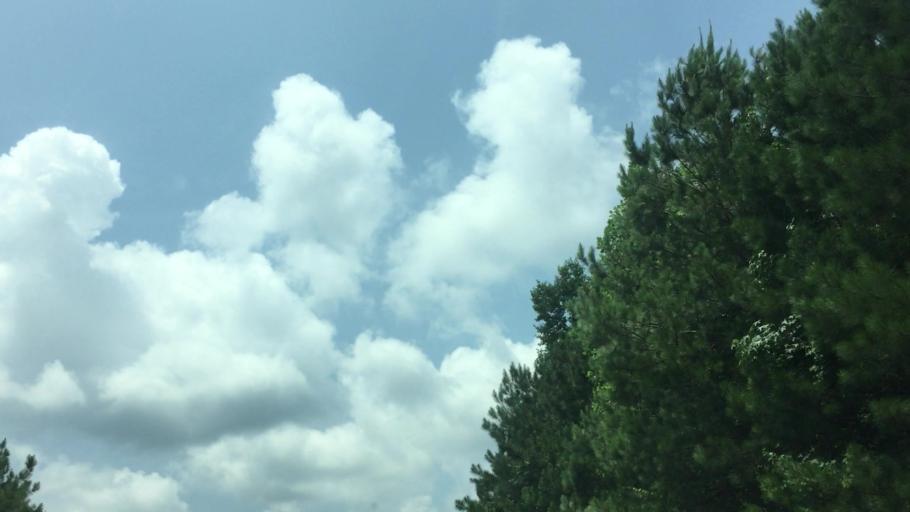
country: US
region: Georgia
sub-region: Fulton County
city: Chattahoochee Hills
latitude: 33.5669
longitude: -84.7133
